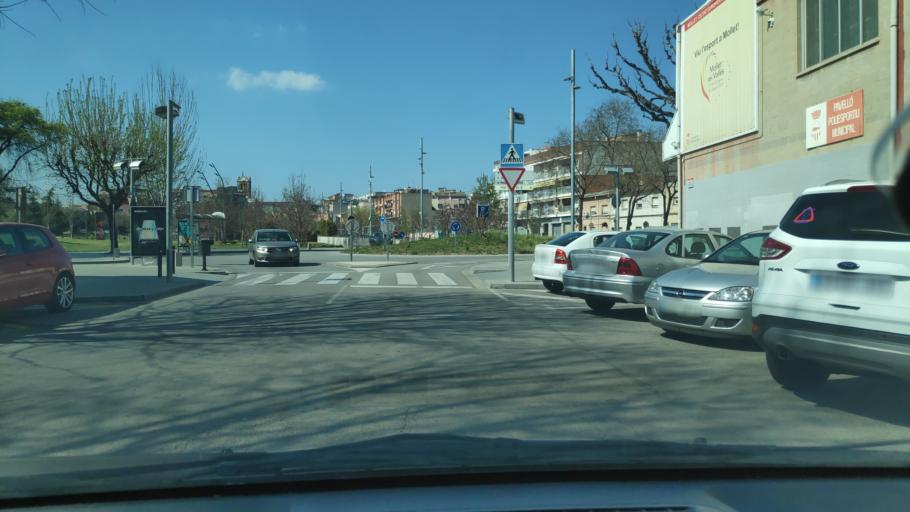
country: ES
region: Catalonia
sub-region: Provincia de Barcelona
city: Mollet del Valles
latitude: 41.5377
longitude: 2.2171
